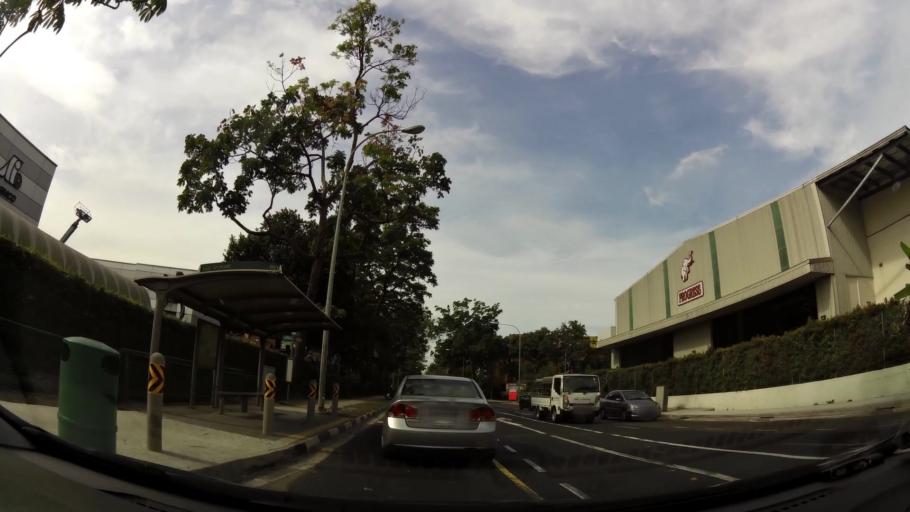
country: MY
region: Johor
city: Johor Bahru
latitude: 1.3193
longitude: 103.6489
